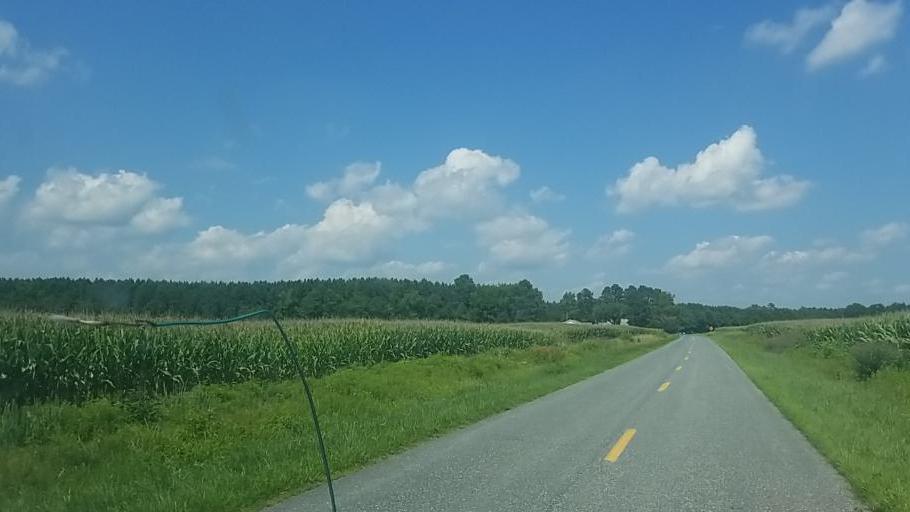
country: US
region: Maryland
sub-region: Wicomico County
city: Hebron
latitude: 38.4353
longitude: -75.8498
